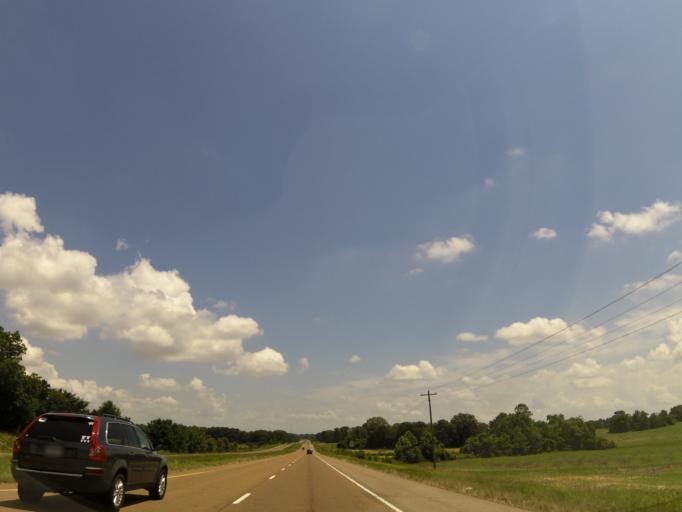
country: US
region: Tennessee
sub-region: Lauderdale County
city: Halls
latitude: 35.9353
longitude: -89.2919
